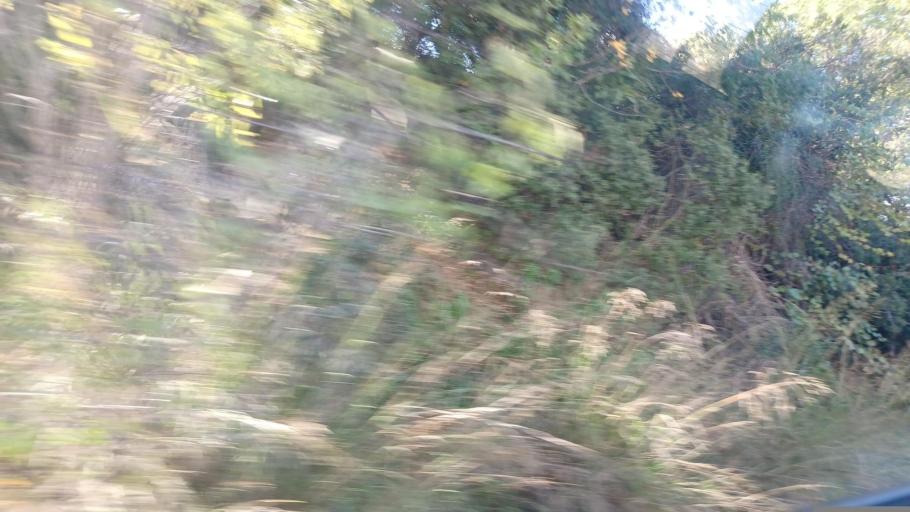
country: CY
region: Pafos
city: Mesogi
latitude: 34.8353
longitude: 32.5488
